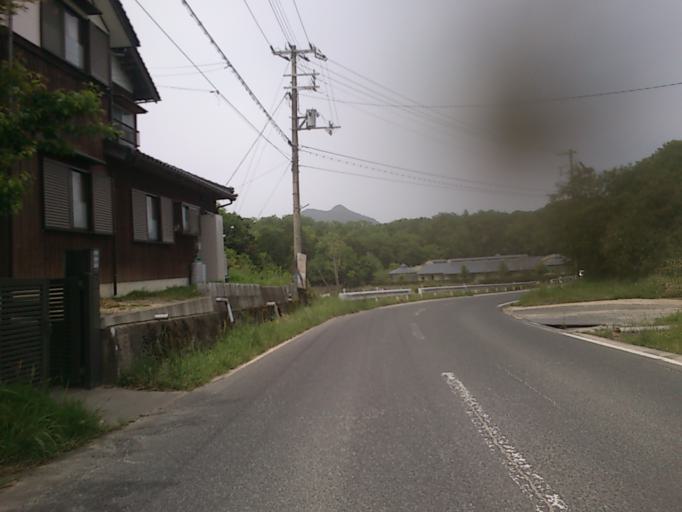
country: JP
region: Kyoto
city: Miyazu
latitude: 35.5959
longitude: 135.0688
